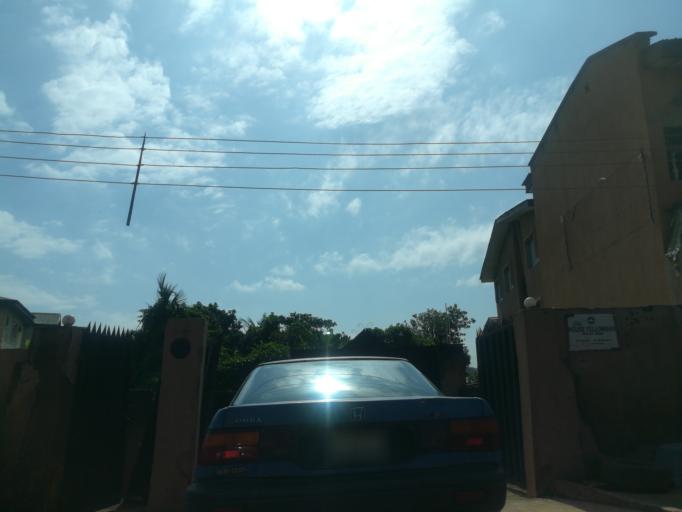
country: NG
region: Oyo
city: Ibadan
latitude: 7.4199
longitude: 3.9764
